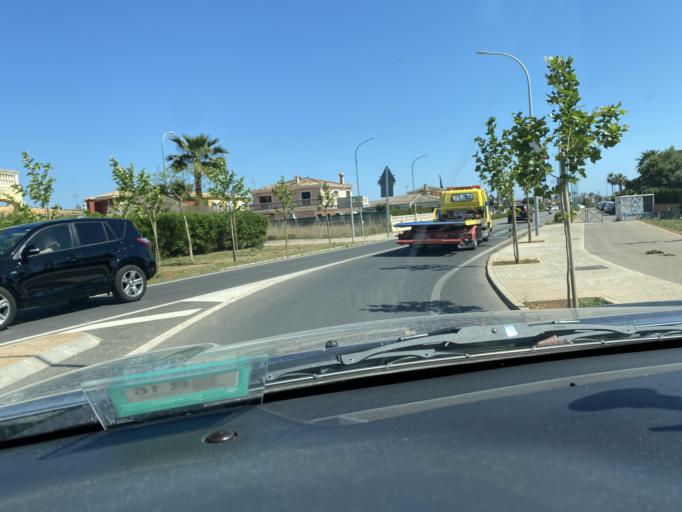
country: ES
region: Balearic Islands
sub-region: Illes Balears
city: Palma
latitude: 39.6138
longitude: 2.6836
